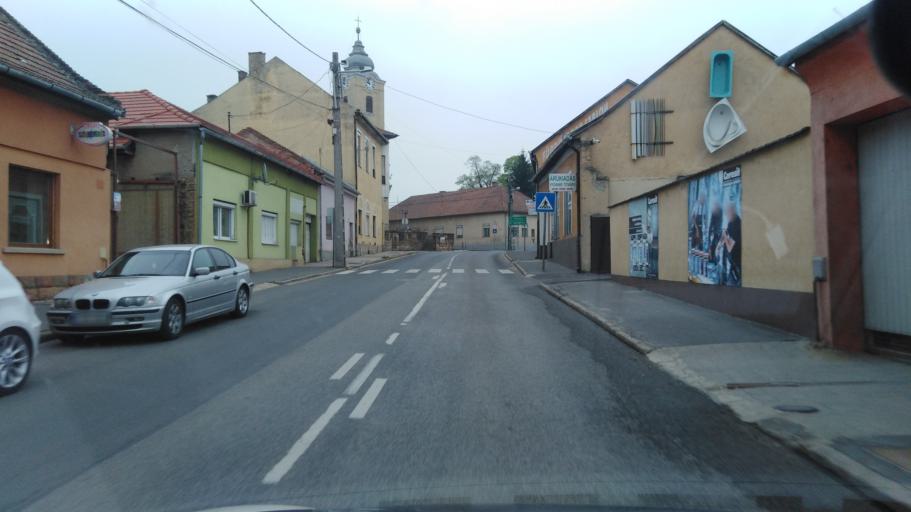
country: HU
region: Nograd
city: Balassagyarmat
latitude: 48.0772
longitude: 19.2957
